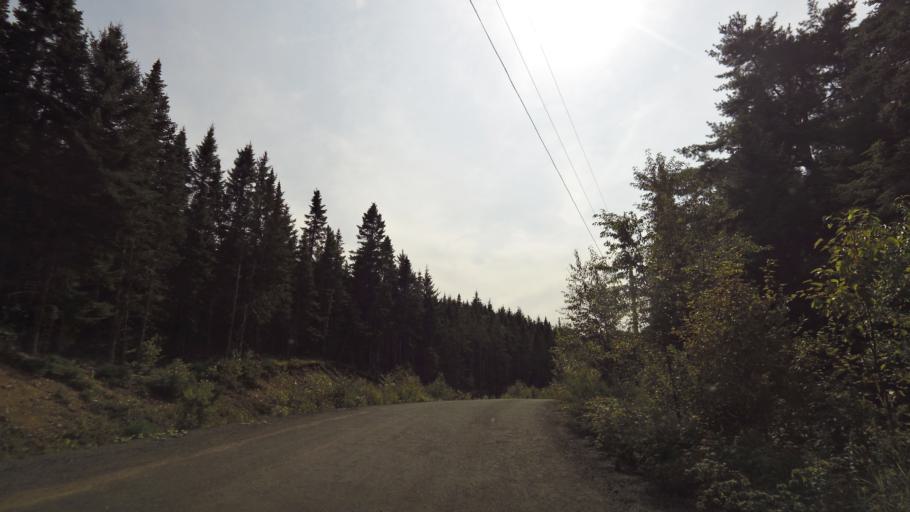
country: CA
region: New Brunswick
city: Hampton
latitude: 45.5774
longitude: -65.8305
